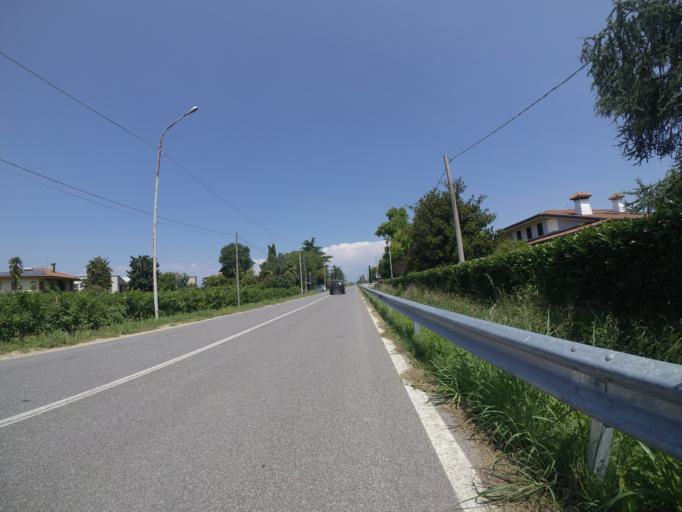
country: IT
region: Friuli Venezia Giulia
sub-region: Provincia di Udine
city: Bertiolo
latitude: 45.9512
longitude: 13.0548
